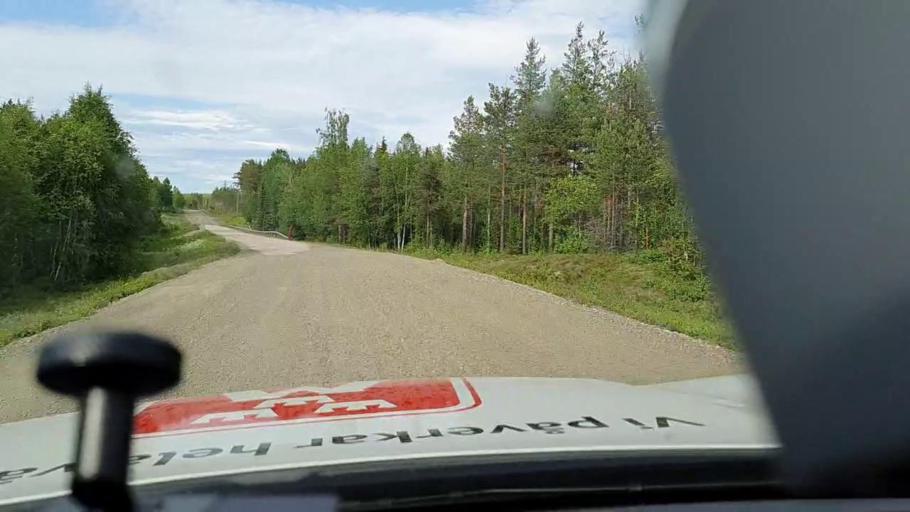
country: SE
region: Norrbotten
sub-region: Alvsbyns Kommun
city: AElvsbyn
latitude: 66.1491
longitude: 21.0297
